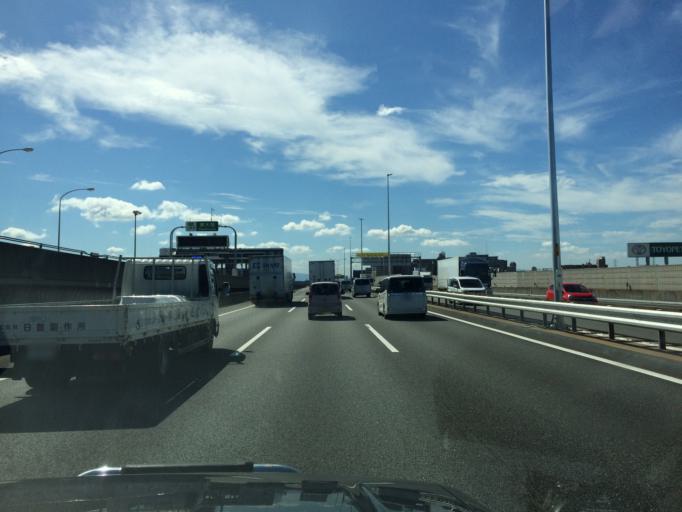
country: JP
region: Osaka
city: Daitocho
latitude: 34.6750
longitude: 135.5978
